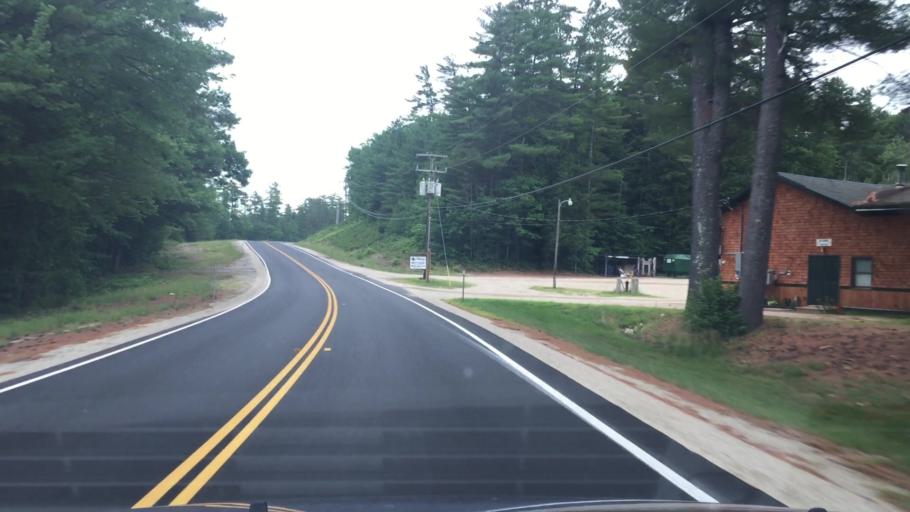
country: US
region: New Hampshire
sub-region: Carroll County
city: Madison
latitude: 43.8731
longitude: -71.0864
